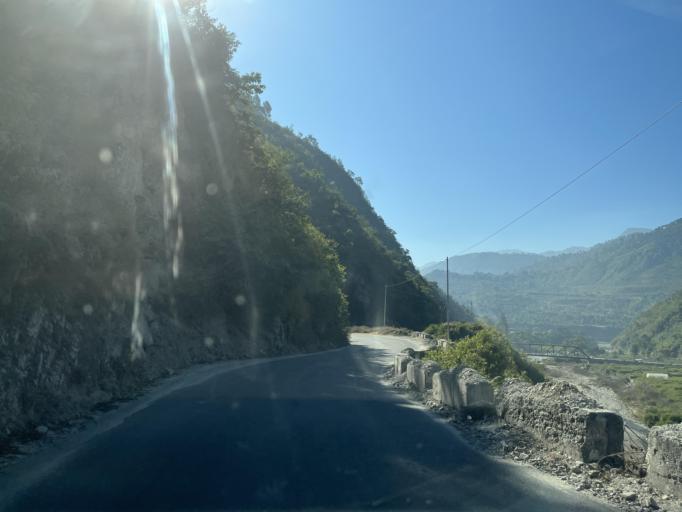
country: IN
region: Uttarakhand
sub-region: Naini Tal
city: Naini Tal
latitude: 29.5187
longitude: 79.4802
